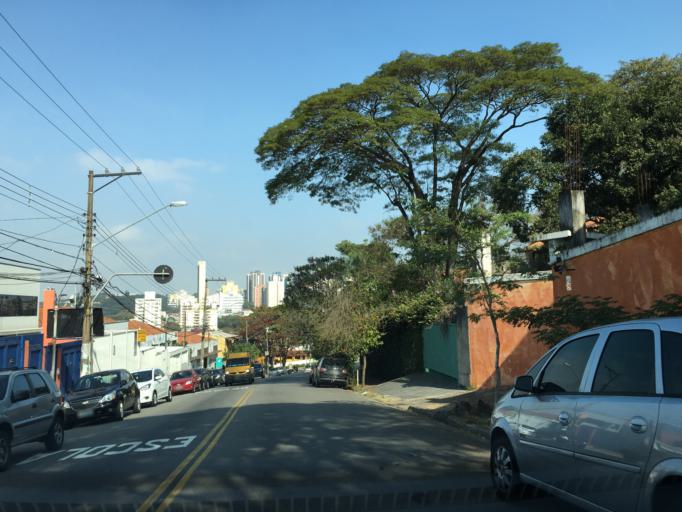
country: BR
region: Sao Paulo
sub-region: Osasco
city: Osasco
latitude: -23.5772
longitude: -46.7207
